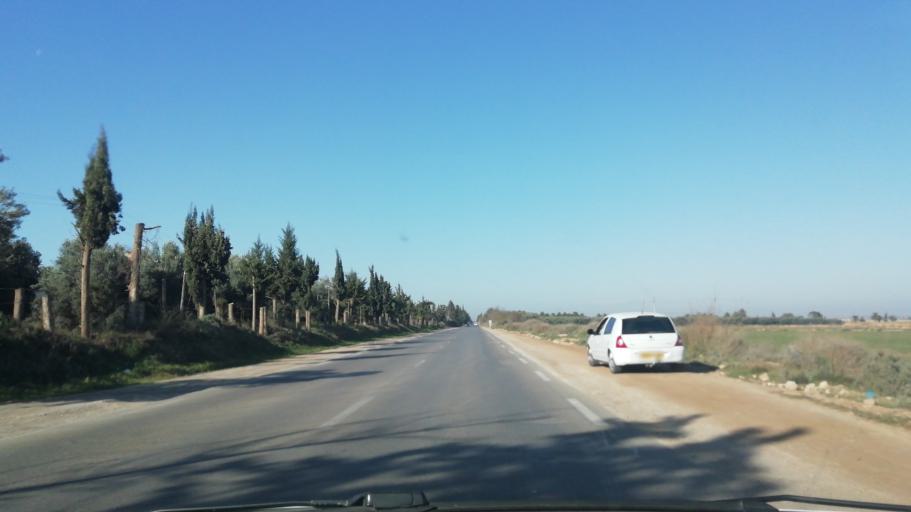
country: DZ
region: Mascara
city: Sig
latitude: 35.5690
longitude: -0.0520
